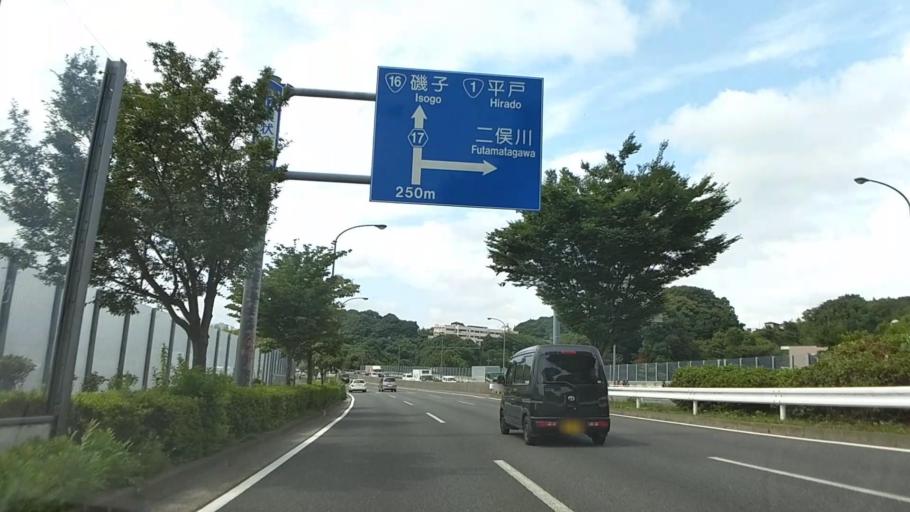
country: JP
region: Kanagawa
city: Yokohama
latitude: 35.4502
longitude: 139.5606
